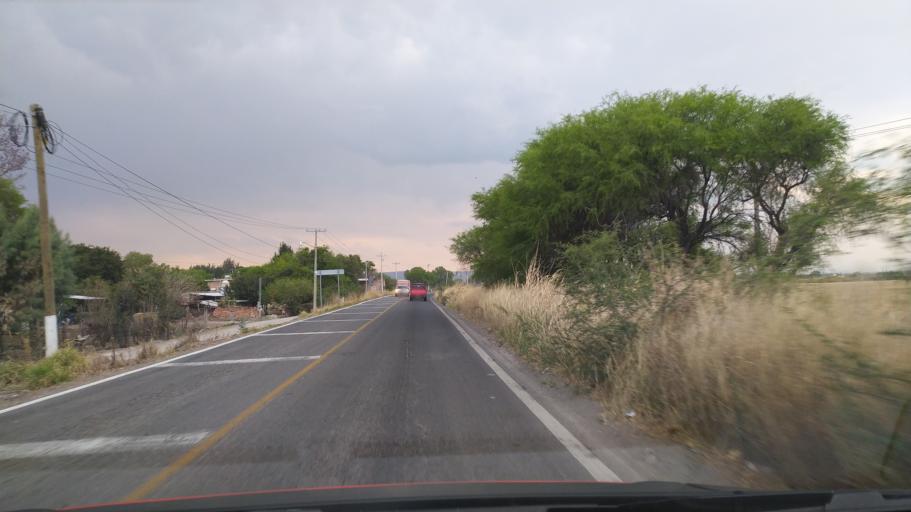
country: MX
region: Guanajuato
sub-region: San Francisco del Rincon
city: San Ignacio de Hidalgo
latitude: 20.8294
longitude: -101.9003
